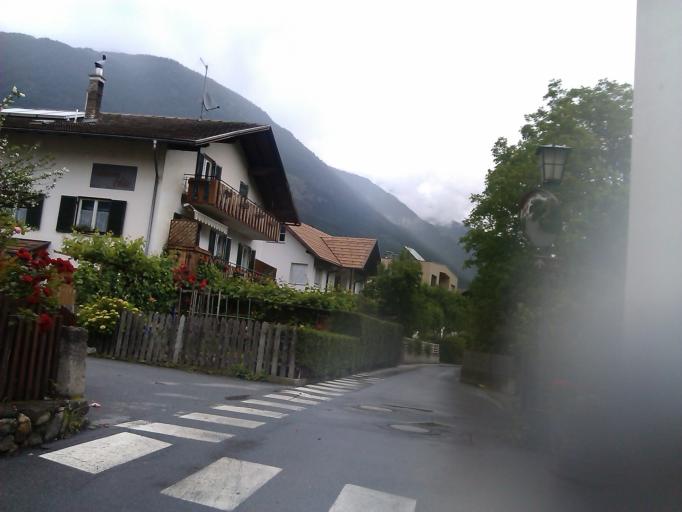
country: IT
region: Trentino-Alto Adige
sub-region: Bolzano
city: Silandro
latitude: 46.6211
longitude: 10.7664
